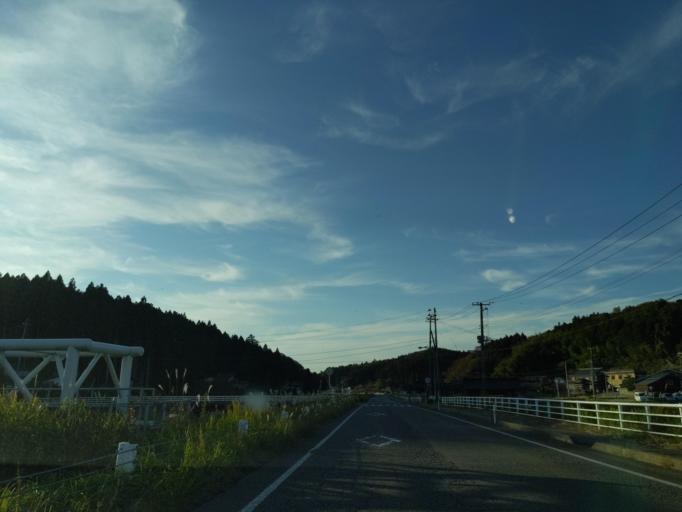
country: JP
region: Niigata
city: Nagaoka
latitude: 37.5718
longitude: 138.7421
